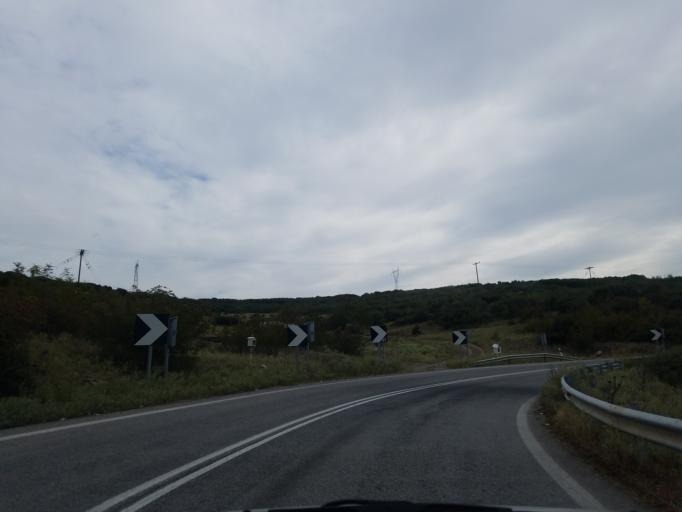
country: GR
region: Central Greece
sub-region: Nomos Fthiotidos
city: Domokos
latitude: 39.1539
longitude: 22.2971
